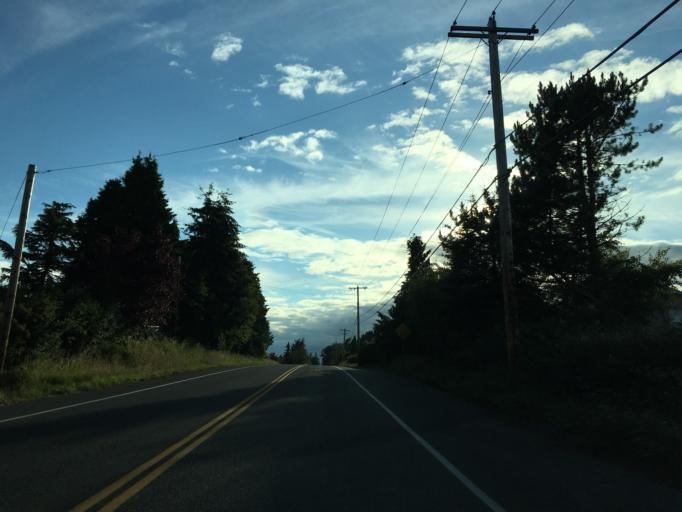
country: US
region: Washington
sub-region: Whatcom County
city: Birch Bay
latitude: 48.9438
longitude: -122.7847
